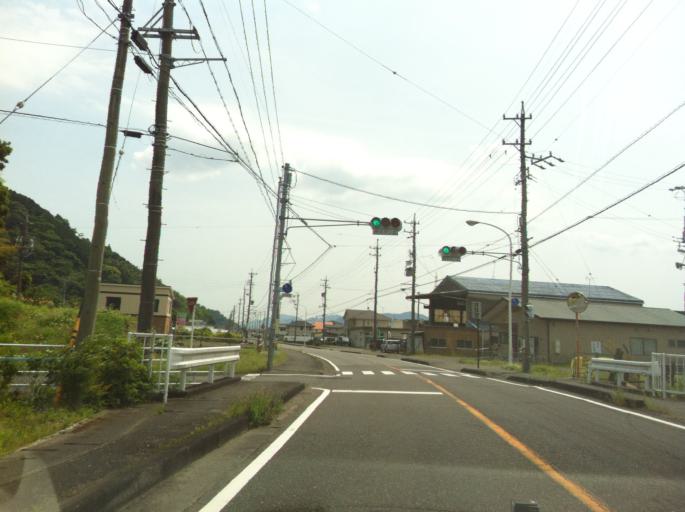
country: JP
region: Shizuoka
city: Shizuoka-shi
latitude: 35.0254
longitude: 138.3766
